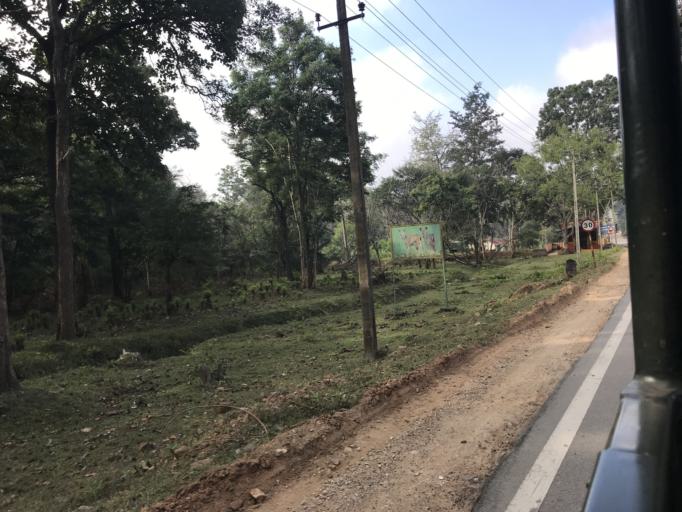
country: IN
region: Karnataka
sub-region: Mysore
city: Heggadadevankote
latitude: 11.9359
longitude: 76.1988
